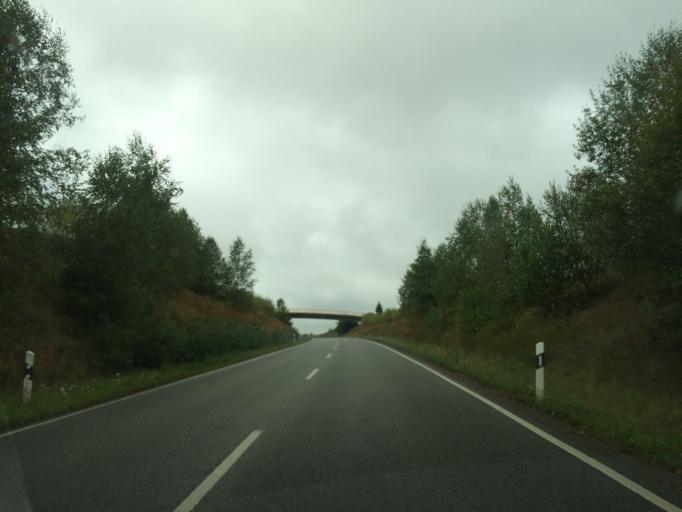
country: DE
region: Rheinland-Pfalz
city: Pirmasens
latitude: 49.1979
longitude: 7.5766
